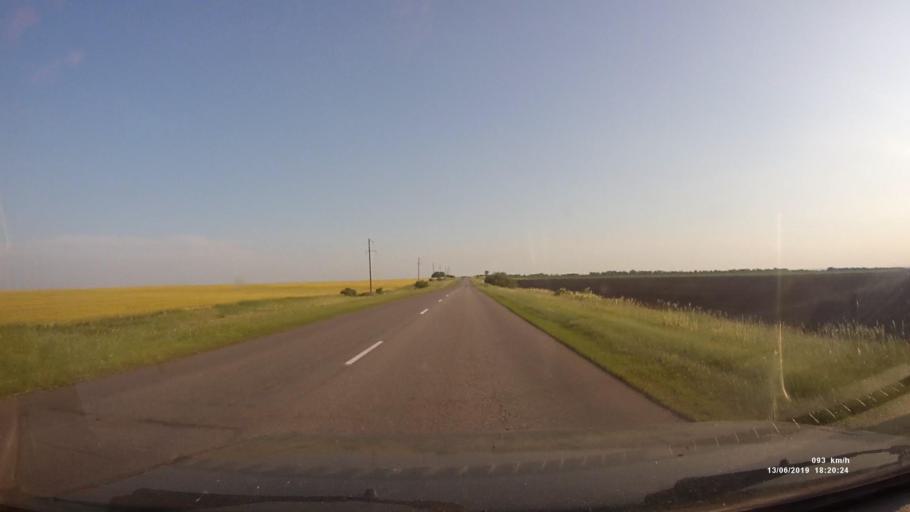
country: RU
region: Rostov
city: Kazanskaya
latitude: 49.8844
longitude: 41.2995
